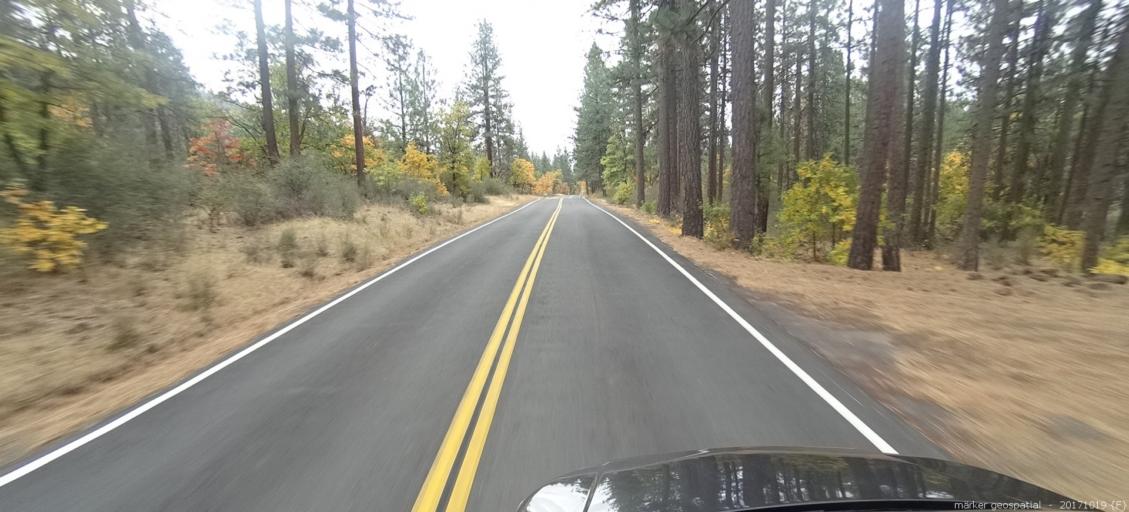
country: US
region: California
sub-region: Shasta County
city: Burney
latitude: 41.1637
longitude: -121.3577
